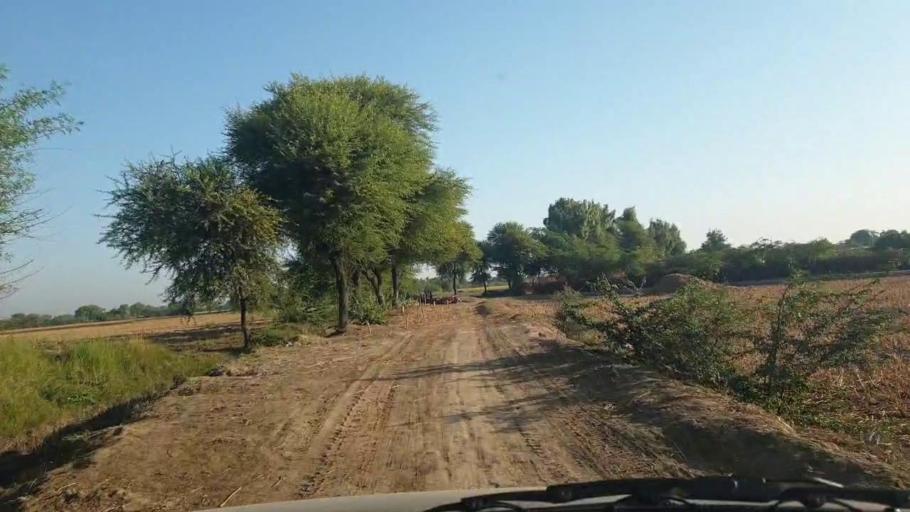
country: PK
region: Sindh
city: Talhar
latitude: 24.7996
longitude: 68.8172
